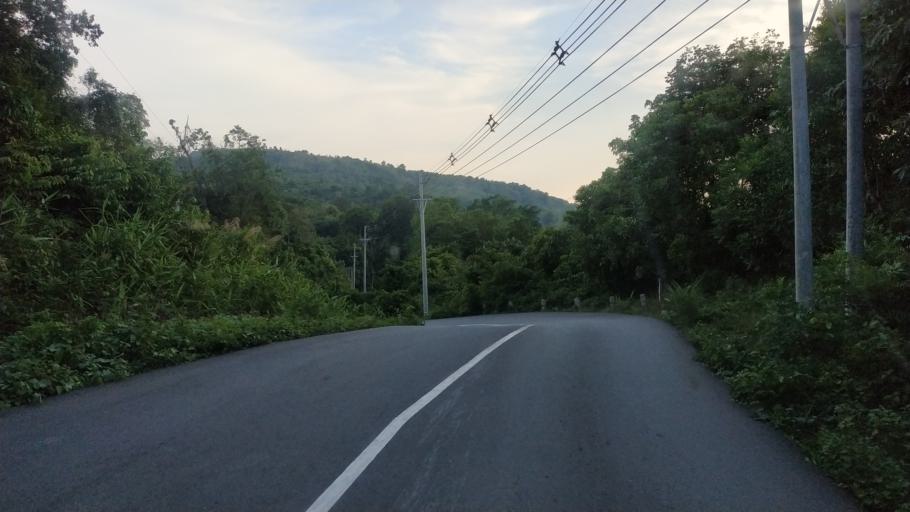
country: MM
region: Mon
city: Kyaikto
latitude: 17.4284
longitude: 97.0886
